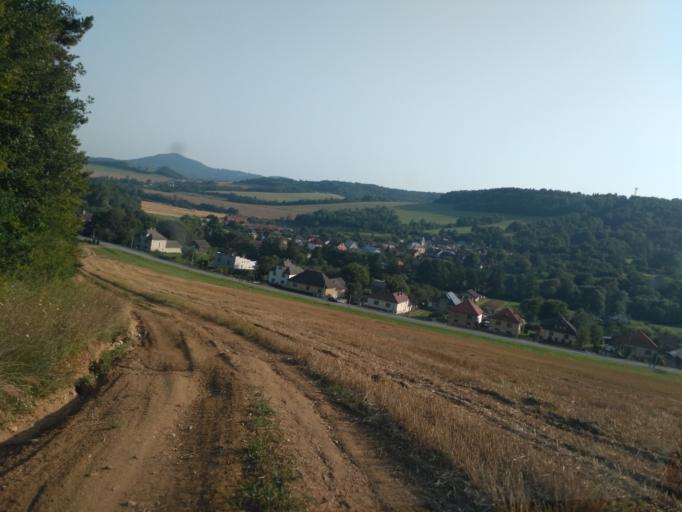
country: SK
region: Presovsky
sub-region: Okres Presov
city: Presov
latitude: 48.9438
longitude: 21.1802
